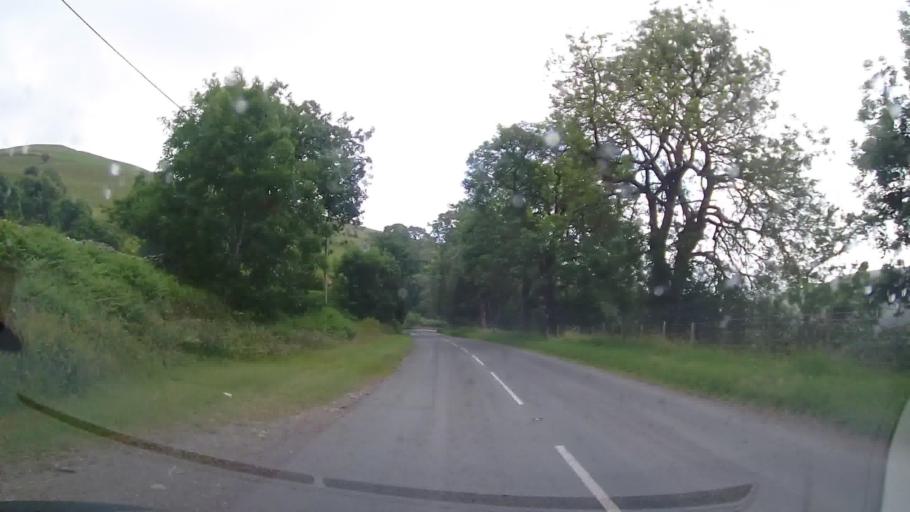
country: GB
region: Wales
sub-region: Sir Powys
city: Llangynog
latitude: 52.8447
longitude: -3.4249
